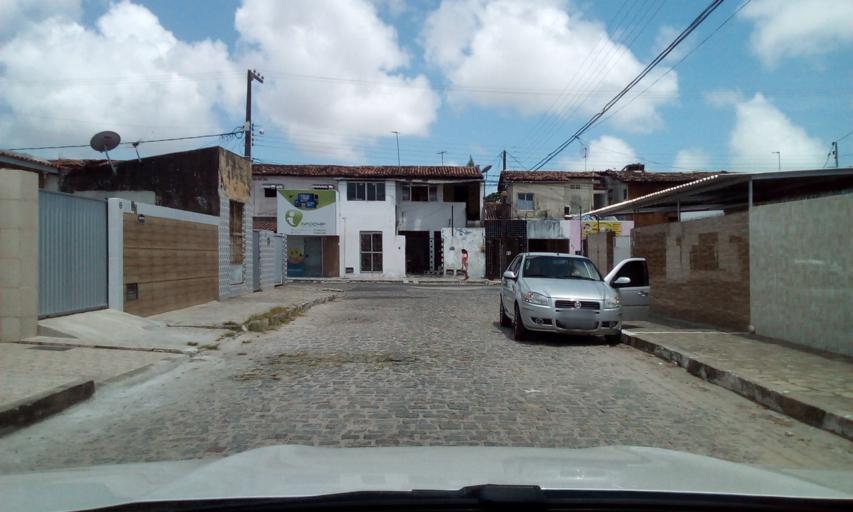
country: BR
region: Paraiba
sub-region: Joao Pessoa
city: Joao Pessoa
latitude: -7.1686
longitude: -34.8395
